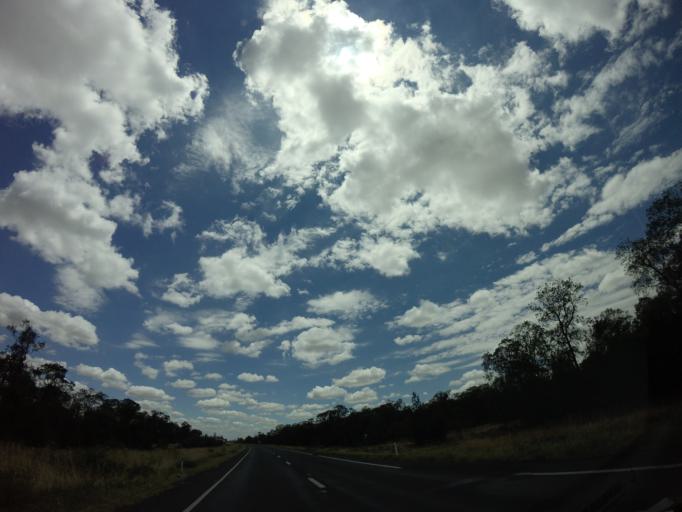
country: AU
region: New South Wales
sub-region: Moree Plains
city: Boggabilla
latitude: -28.9192
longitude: 150.1279
